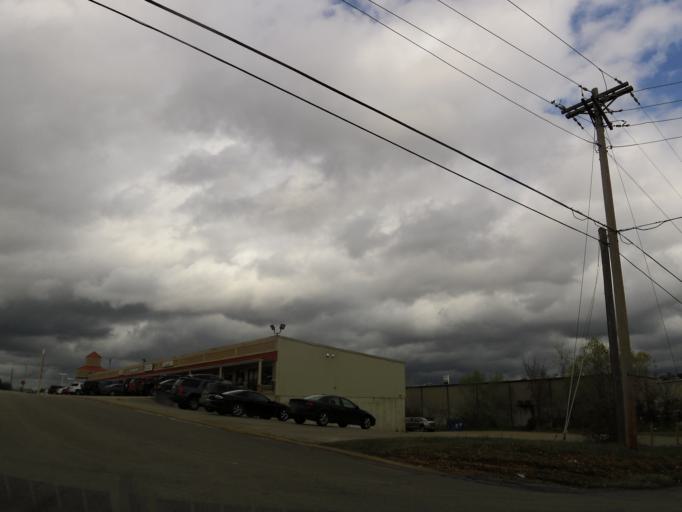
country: US
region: Missouri
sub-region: Butler County
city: Poplar Bluff
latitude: 36.7512
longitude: -90.4080
